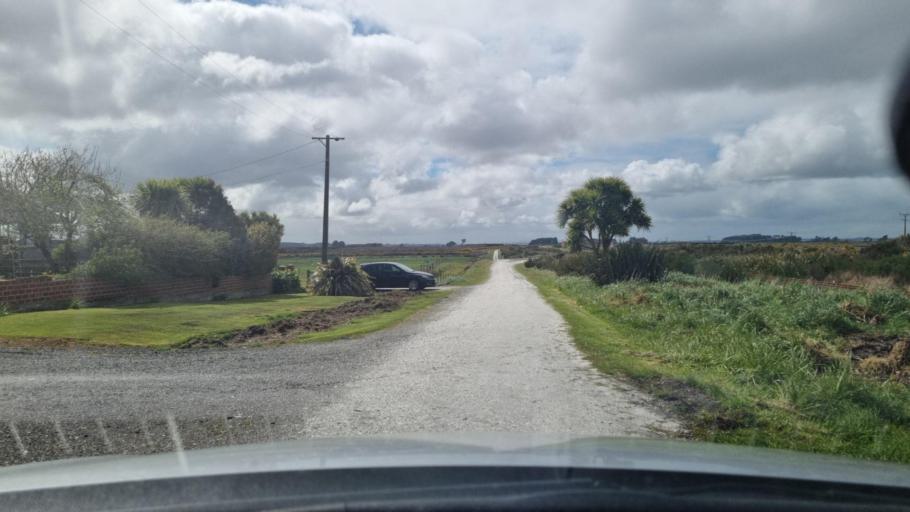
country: NZ
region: Southland
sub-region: Invercargill City
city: Bluff
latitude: -46.5364
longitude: 168.3036
